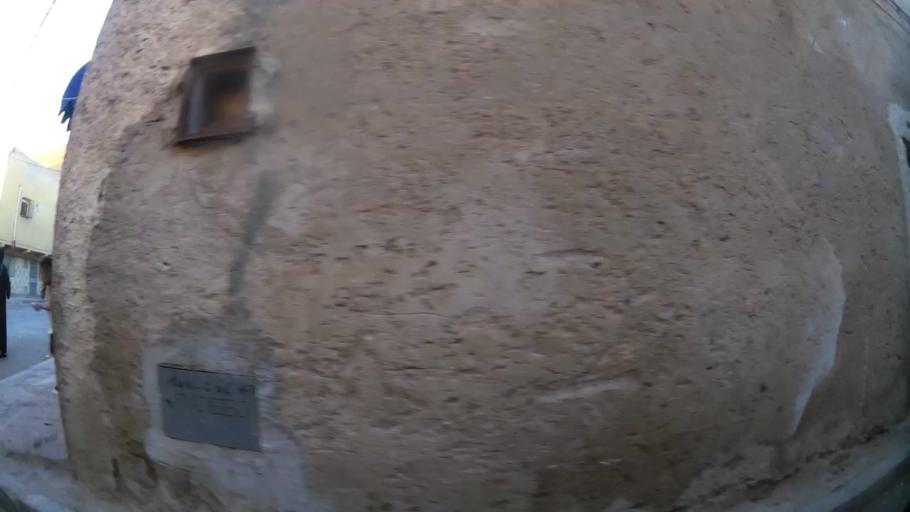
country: MA
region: Oriental
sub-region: Oujda-Angad
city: Oujda
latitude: 34.7046
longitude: -1.9223
